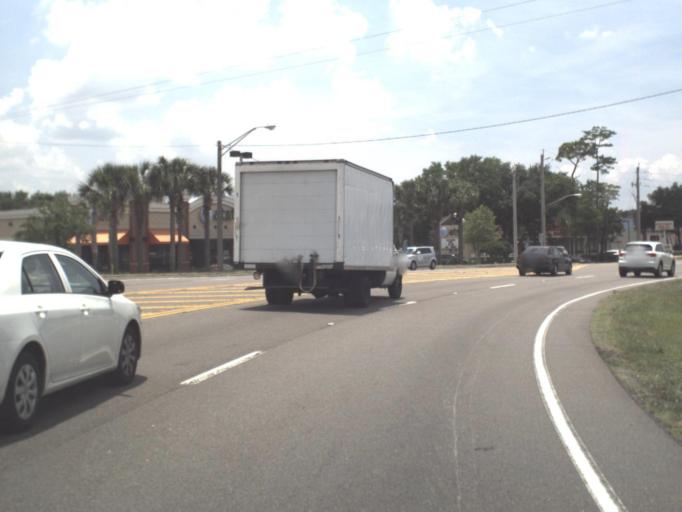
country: US
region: Florida
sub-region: Duval County
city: Jacksonville
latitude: 30.3209
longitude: -81.5517
